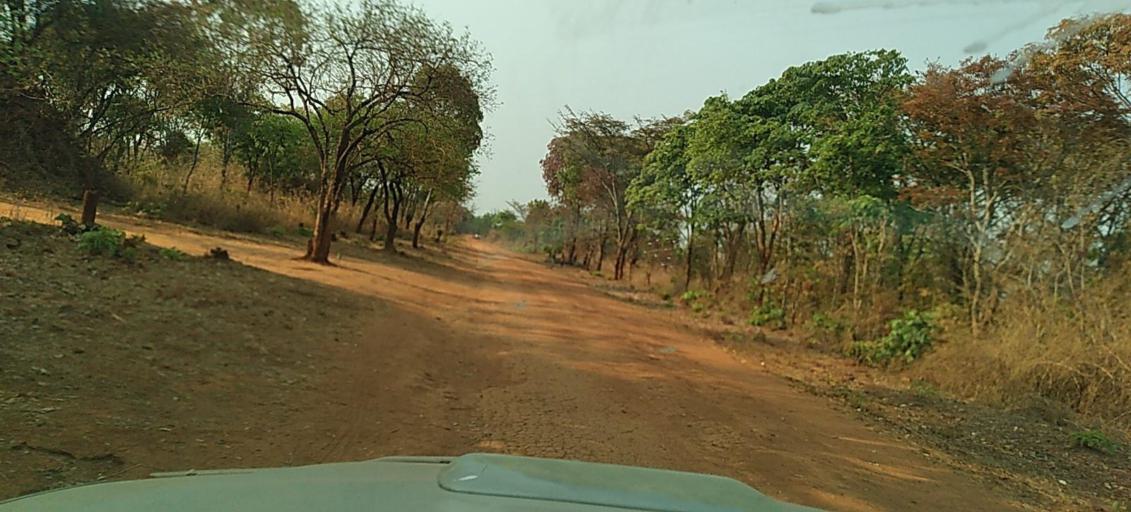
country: ZM
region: North-Western
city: Kasempa
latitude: -13.2983
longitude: 26.5542
